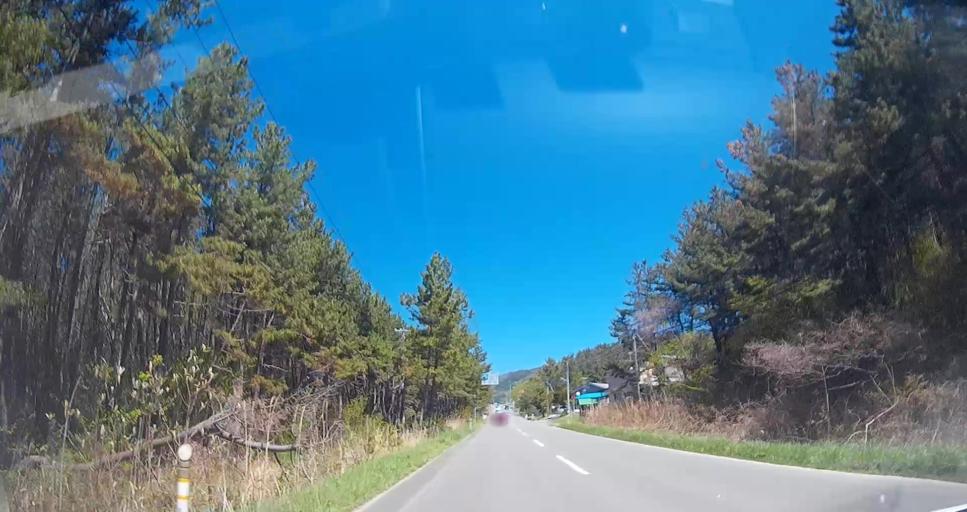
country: JP
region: Aomori
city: Mutsu
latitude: 41.3775
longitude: 141.3948
